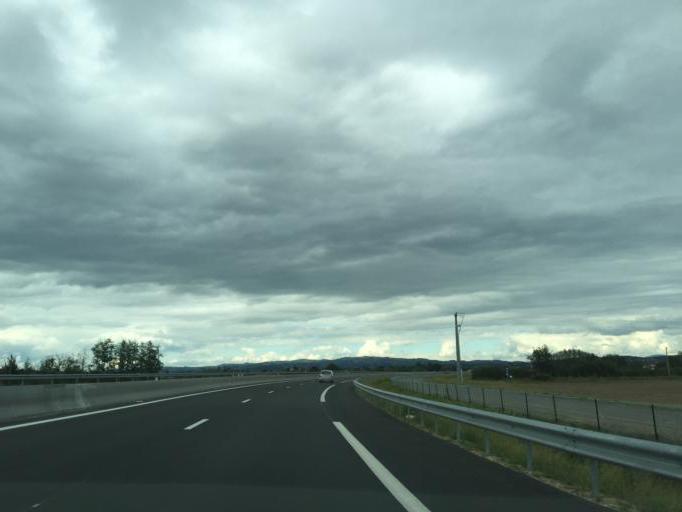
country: FR
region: Rhone-Alpes
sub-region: Departement de la Loire
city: Bonson
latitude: 45.5148
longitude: 4.1988
